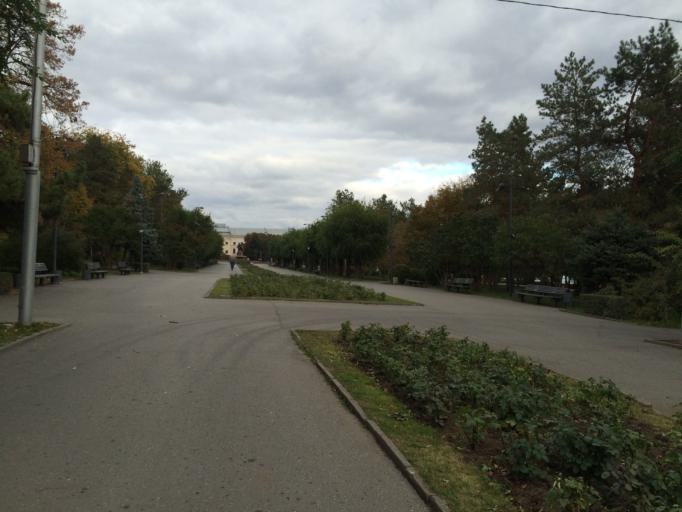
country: RU
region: Volgograd
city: Volgograd
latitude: 48.7035
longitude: 44.5184
